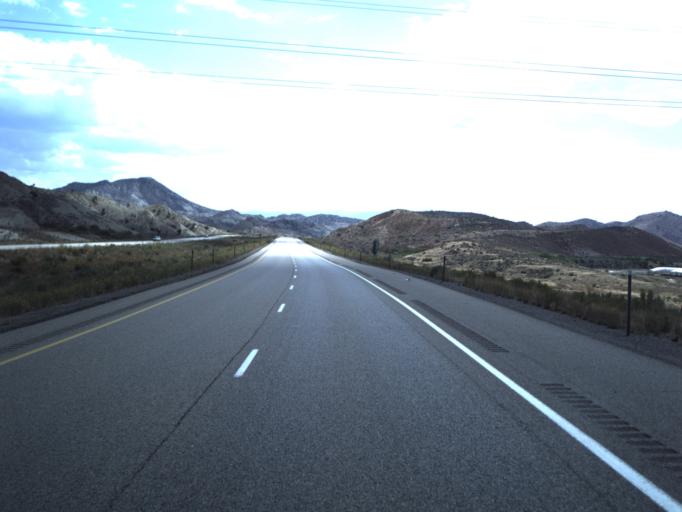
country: US
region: Utah
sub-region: Sevier County
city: Aurora
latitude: 38.9002
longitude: -111.9045
